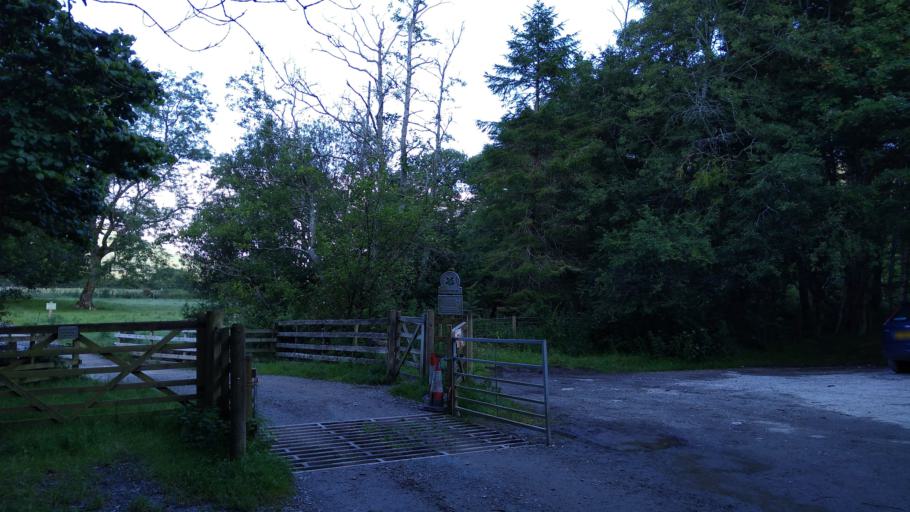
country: GB
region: England
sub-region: Cumbria
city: Cockermouth
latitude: 54.5772
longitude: -3.3405
